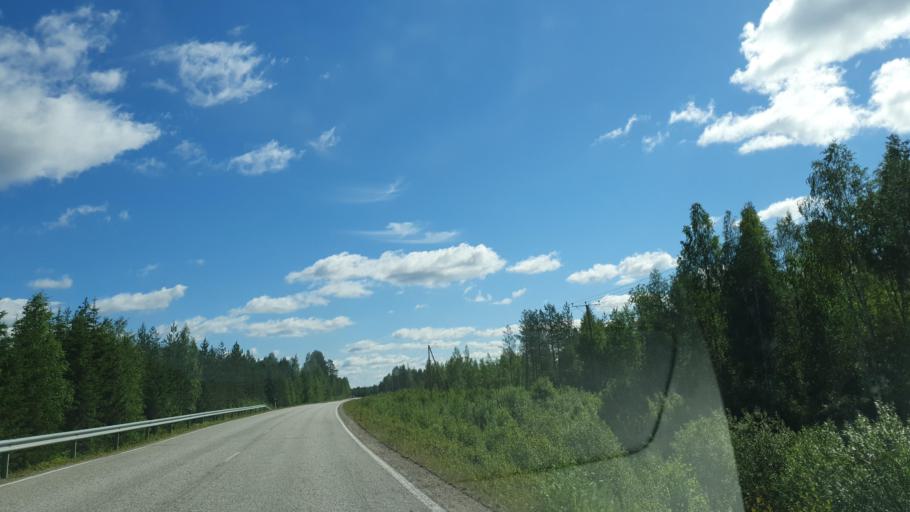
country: FI
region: Kainuu
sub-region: Kehys-Kainuu
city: Kuhmo
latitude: 64.2166
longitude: 29.7728
